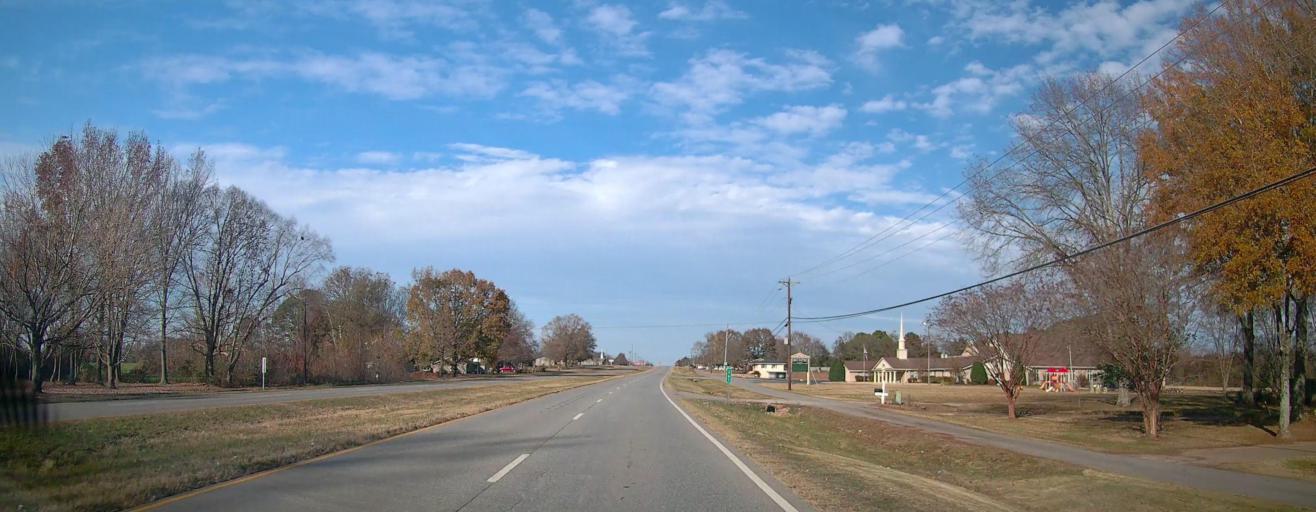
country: US
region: Alabama
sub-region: Limestone County
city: Athens
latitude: 34.7240
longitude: -86.9570
